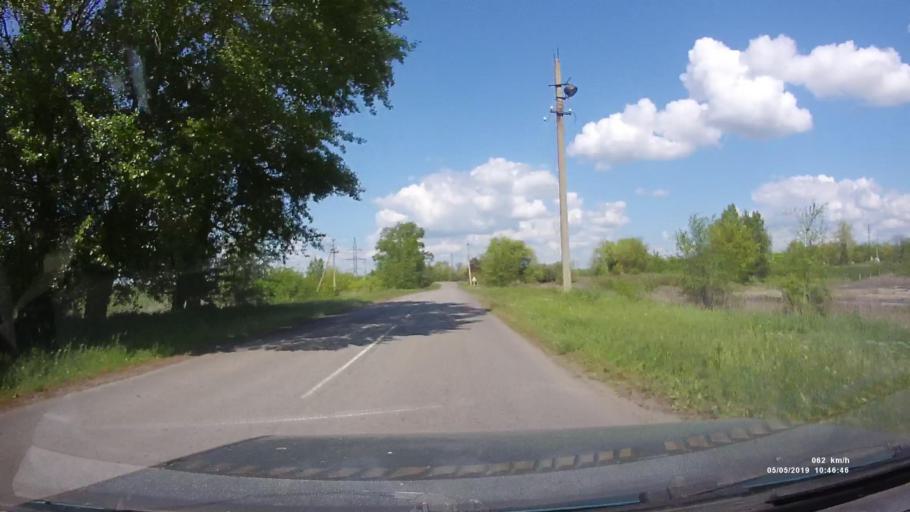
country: RU
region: Rostov
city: Ust'-Donetskiy
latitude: 47.6359
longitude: 40.8410
